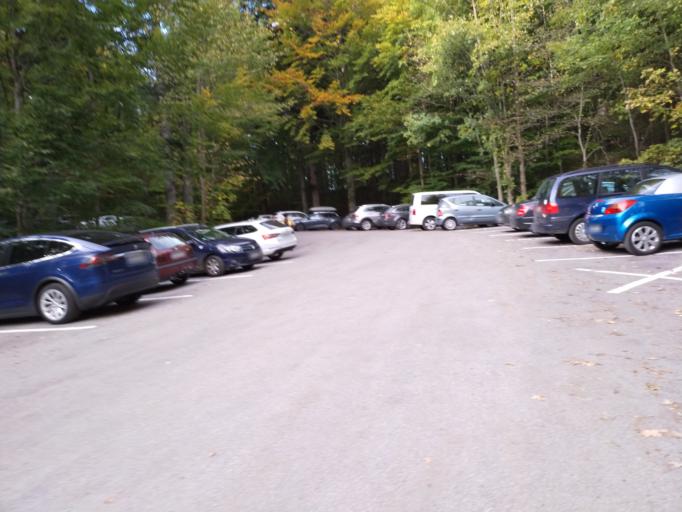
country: AT
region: Tyrol
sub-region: Politischer Bezirk Reutte
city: Vils
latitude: 47.5631
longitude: 10.6401
